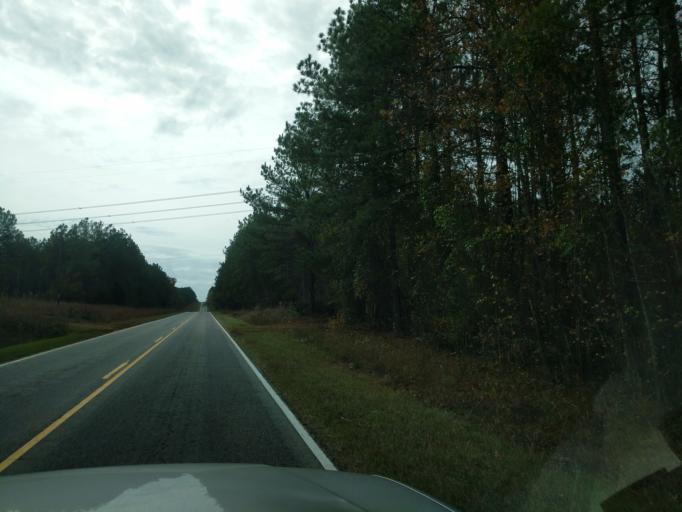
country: US
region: South Carolina
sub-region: Laurens County
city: Joanna
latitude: 34.3097
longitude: -81.8432
